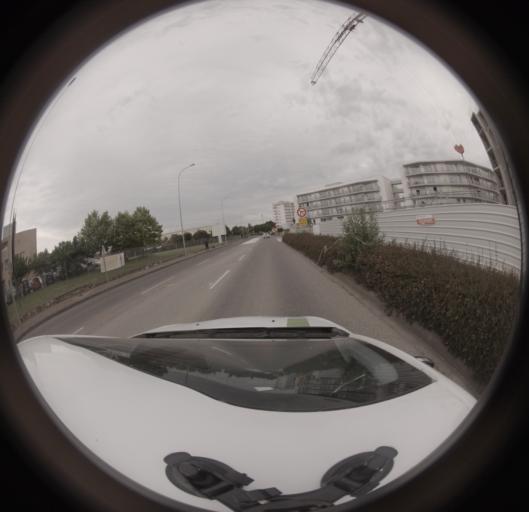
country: FR
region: Midi-Pyrenees
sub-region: Departement du Tarn-et-Garonne
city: Montauban
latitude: 44.0101
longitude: 1.3746
